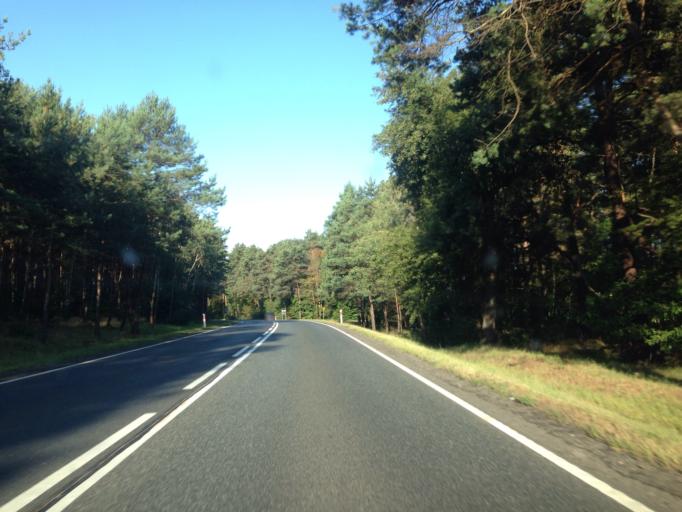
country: PL
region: Kujawsko-Pomorskie
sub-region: Powiat bydgoski
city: Nowa Wies Wielka
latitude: 53.0653
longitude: 18.1142
